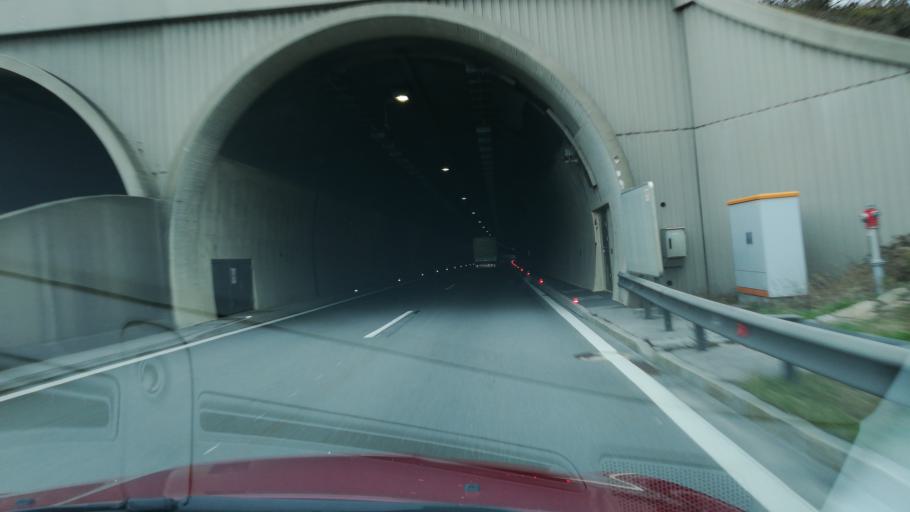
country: AT
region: Upper Austria
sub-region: Politischer Bezirk Kirchdorf an der Krems
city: Kremsmunster
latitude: 48.0012
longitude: 14.0794
